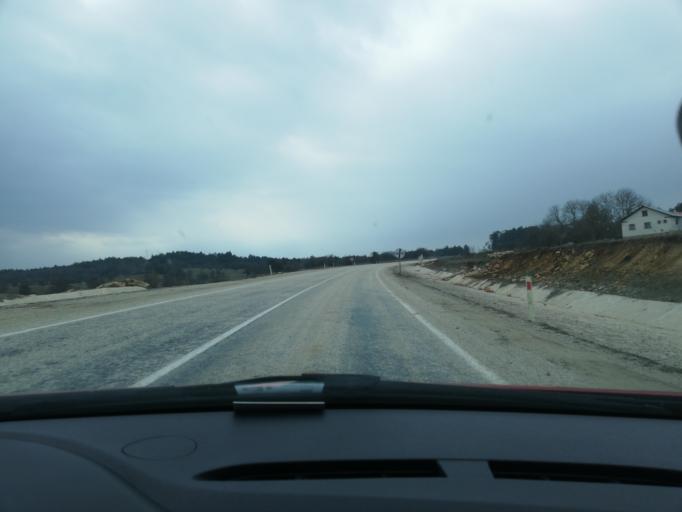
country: TR
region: Karabuk
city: Eflani
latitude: 41.4921
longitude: 33.0491
